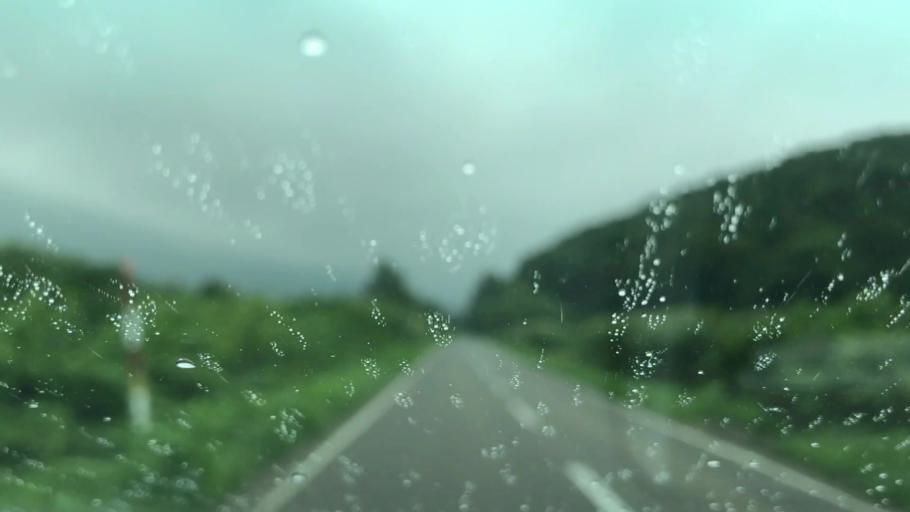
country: JP
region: Hokkaido
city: Iwanai
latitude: 42.7458
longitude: 140.2888
